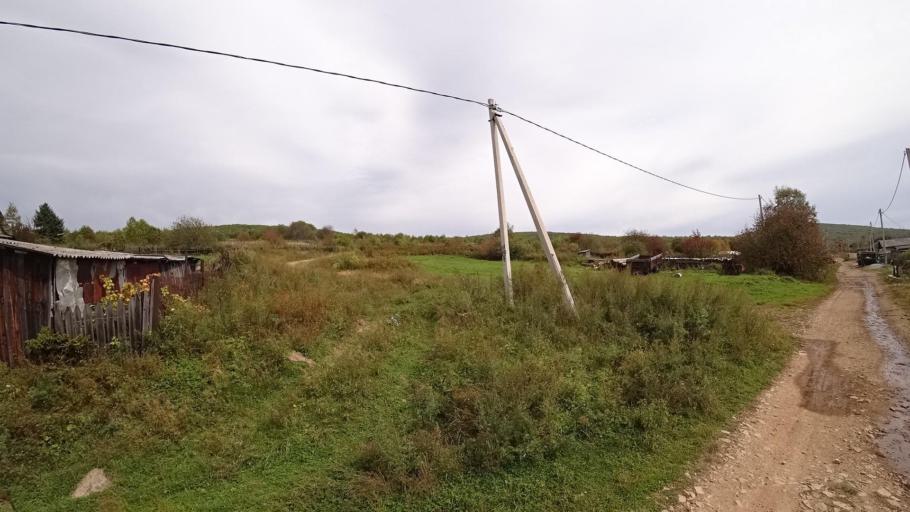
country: RU
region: Jewish Autonomous Oblast
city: Khingansk
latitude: 49.1236
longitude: 131.2065
